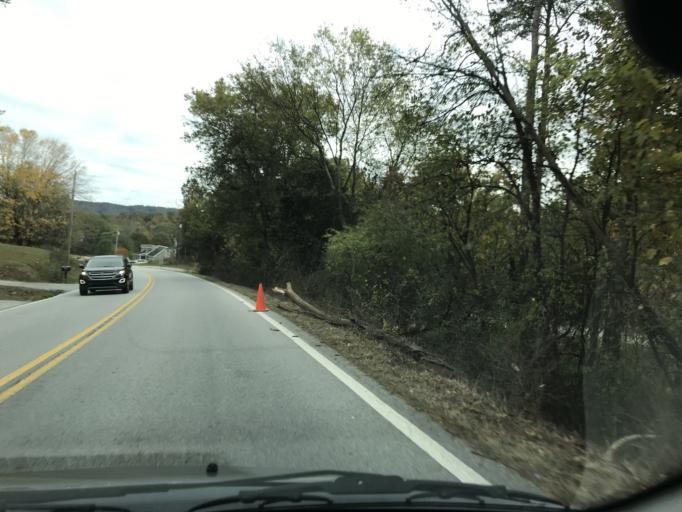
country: US
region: Tennessee
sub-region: Hamilton County
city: Lakesite
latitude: 35.1822
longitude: -85.0568
